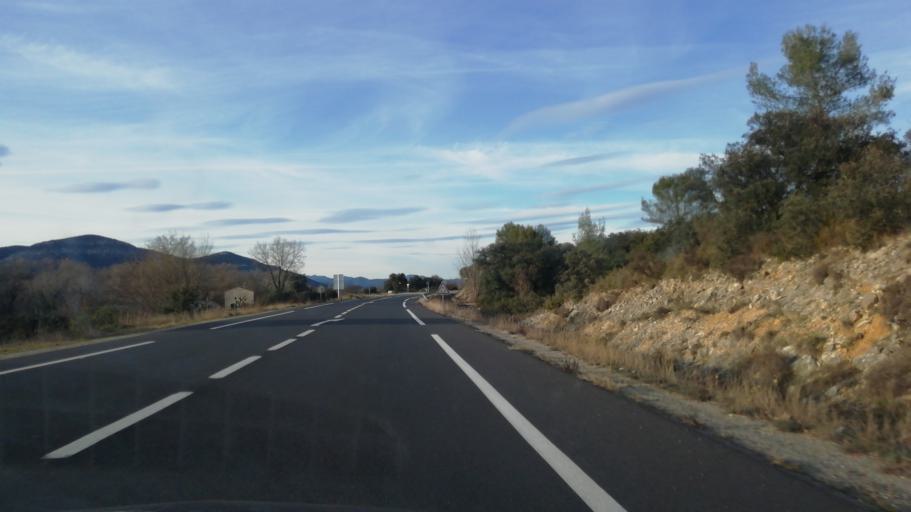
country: FR
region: Languedoc-Roussillon
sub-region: Departement du Gard
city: Quissac
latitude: 43.8905
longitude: 4.0130
